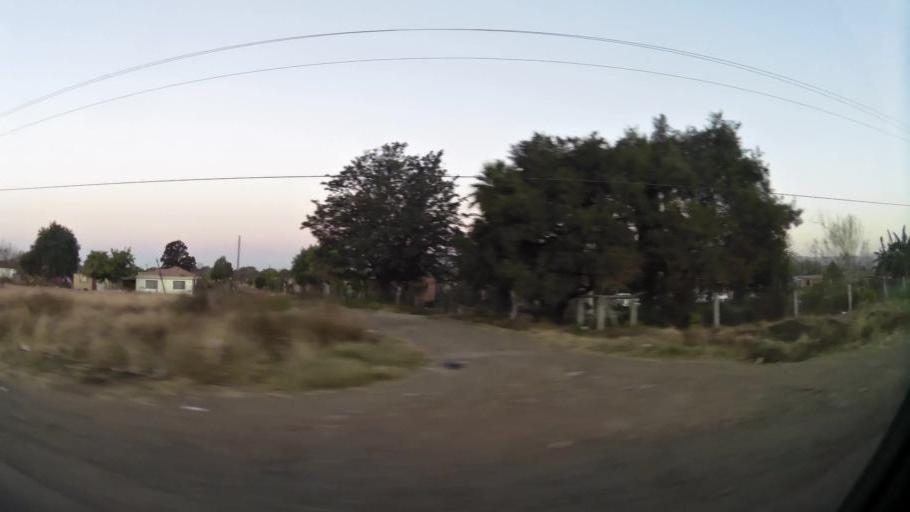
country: ZA
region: North-West
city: Ga-Rankuwa
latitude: -25.6096
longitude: 27.9653
